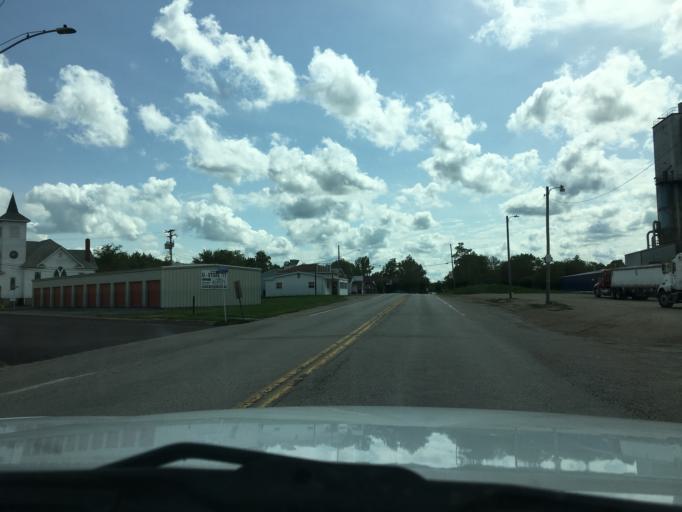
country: US
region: Missouri
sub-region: Franklin County
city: Gerald
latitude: 38.4006
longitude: -91.3318
